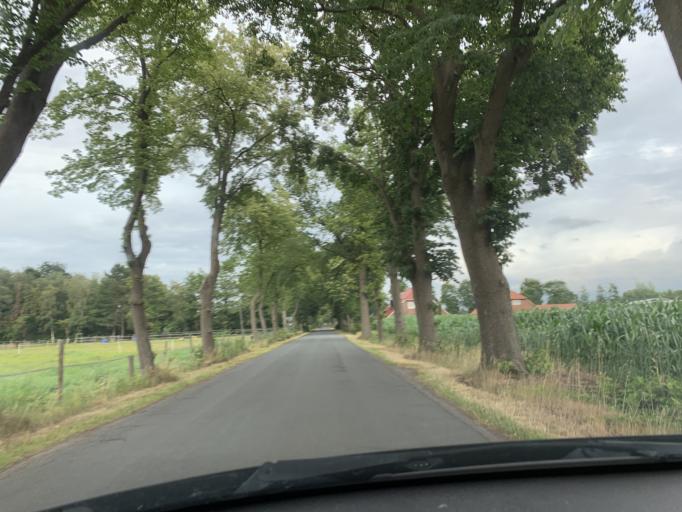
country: DE
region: Lower Saxony
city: Westerstede
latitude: 53.2567
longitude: 7.8937
